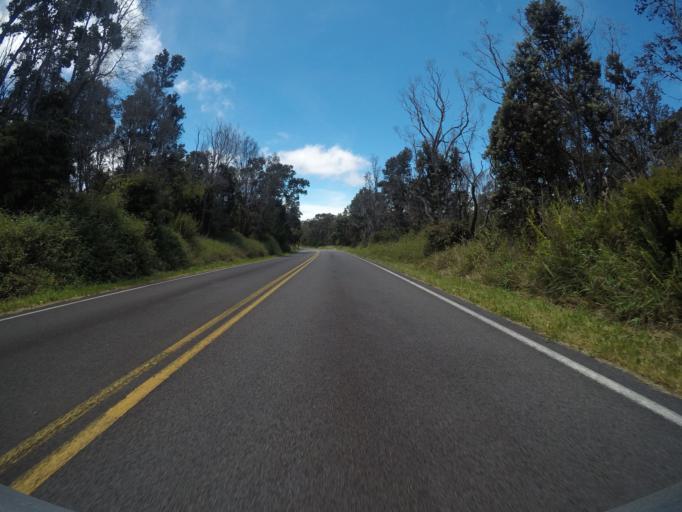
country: US
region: Hawaii
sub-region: Hawaii County
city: Volcano
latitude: 19.3884
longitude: -155.2467
